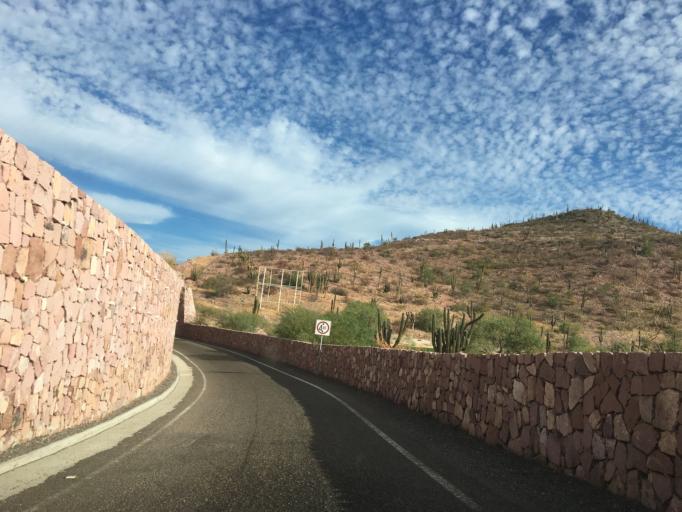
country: MX
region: Baja California Sur
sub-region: La Paz
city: La Paz
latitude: 24.2133
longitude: -110.2947
